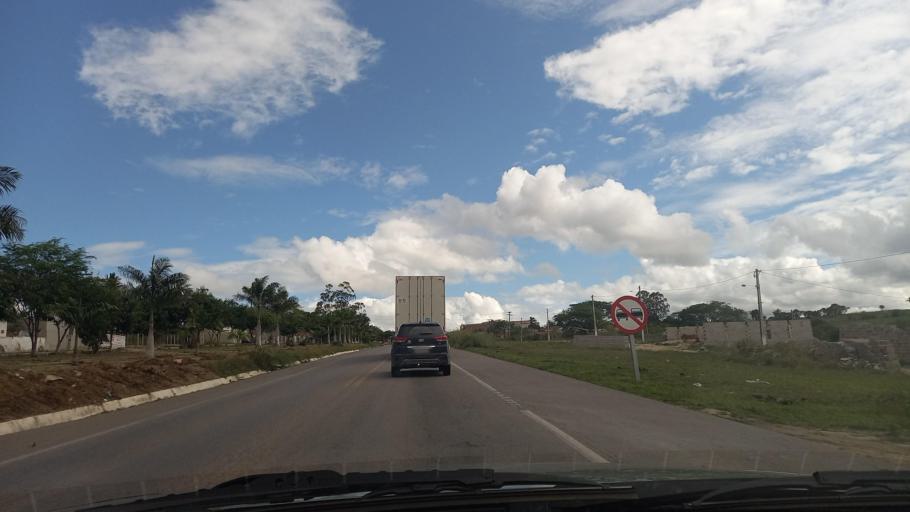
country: BR
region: Pernambuco
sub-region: Lajedo
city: Lajedo
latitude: -8.7058
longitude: -36.4175
